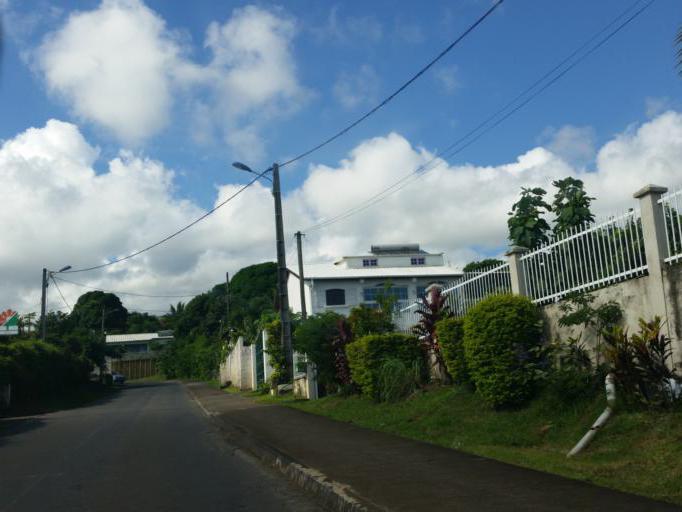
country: RE
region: Reunion
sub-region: Reunion
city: Sainte-Marie
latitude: -20.9161
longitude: 55.5329
